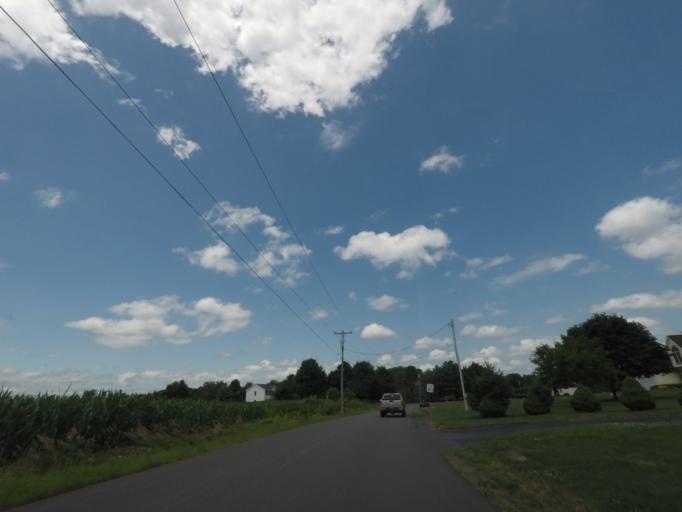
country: US
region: New York
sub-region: Rensselaer County
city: East Greenbush
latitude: 42.5394
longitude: -73.6926
